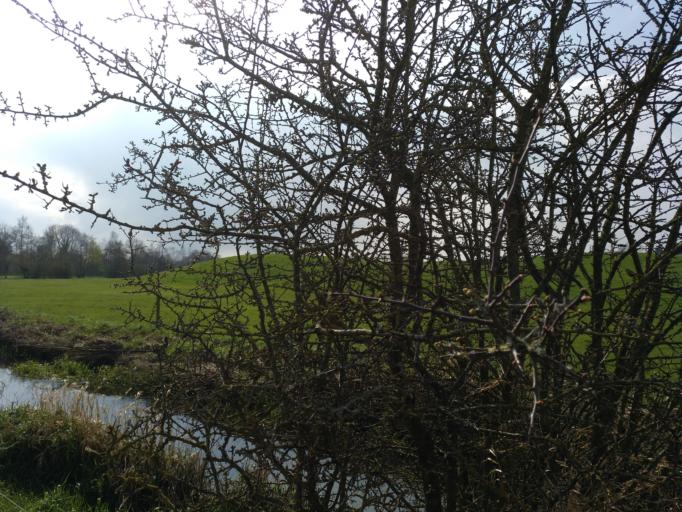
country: IE
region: Ulster
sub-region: County Monaghan
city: Clones
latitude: 54.2112
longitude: -7.1187
